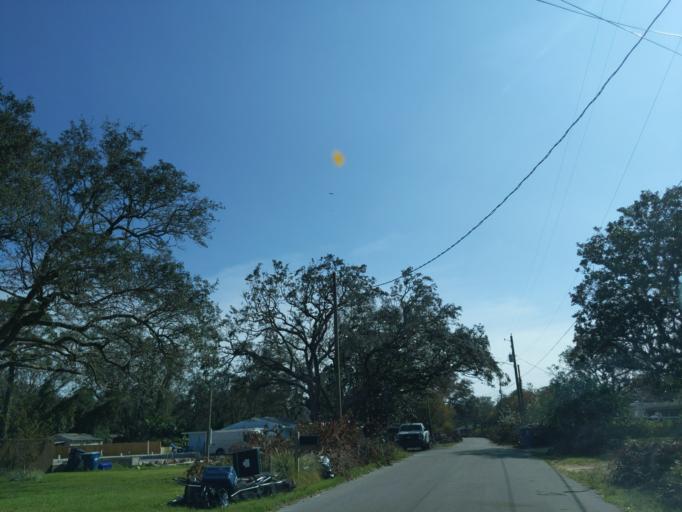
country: US
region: Florida
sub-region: Santa Rosa County
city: Gulf Breeze
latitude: 30.3593
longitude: -87.1927
